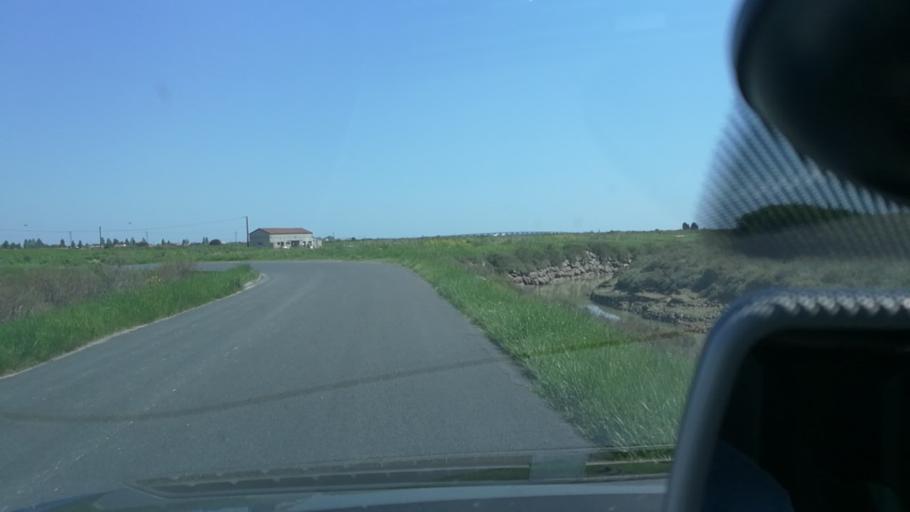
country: FR
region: Poitou-Charentes
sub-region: Departement de la Charente-Maritime
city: Saint-Trojan-les-Bains
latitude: 45.8661
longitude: -1.2220
